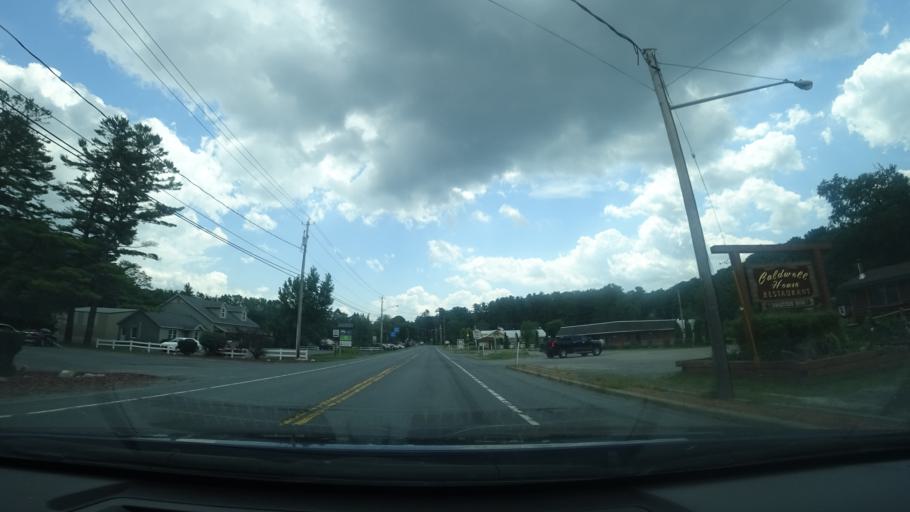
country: US
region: New York
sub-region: Warren County
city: Glens Falls North
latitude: 43.3896
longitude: -73.7044
